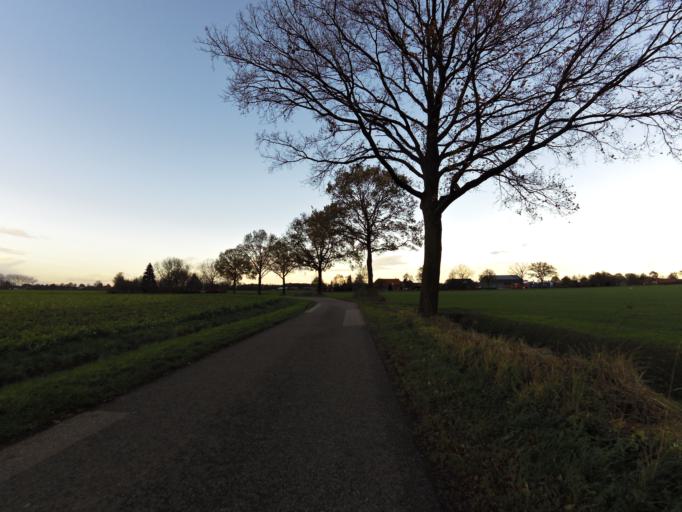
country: NL
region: Gelderland
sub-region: Oude IJsselstreek
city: Gendringen
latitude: 51.8459
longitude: 6.3833
